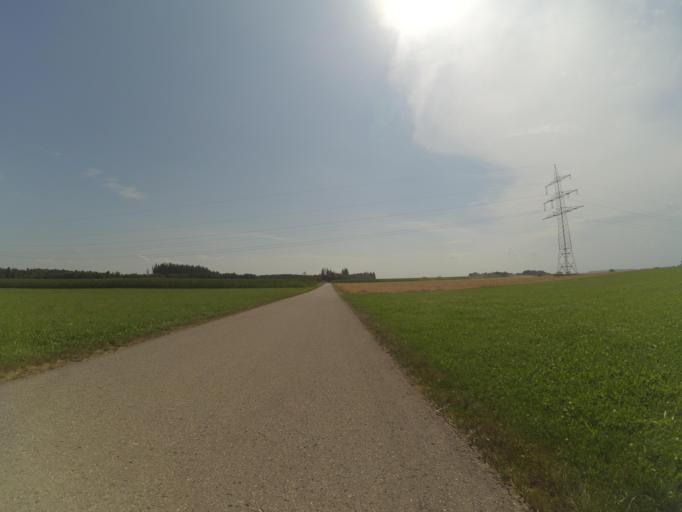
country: DE
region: Bavaria
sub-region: Swabia
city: Buchloe
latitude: 48.0234
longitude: 10.7377
